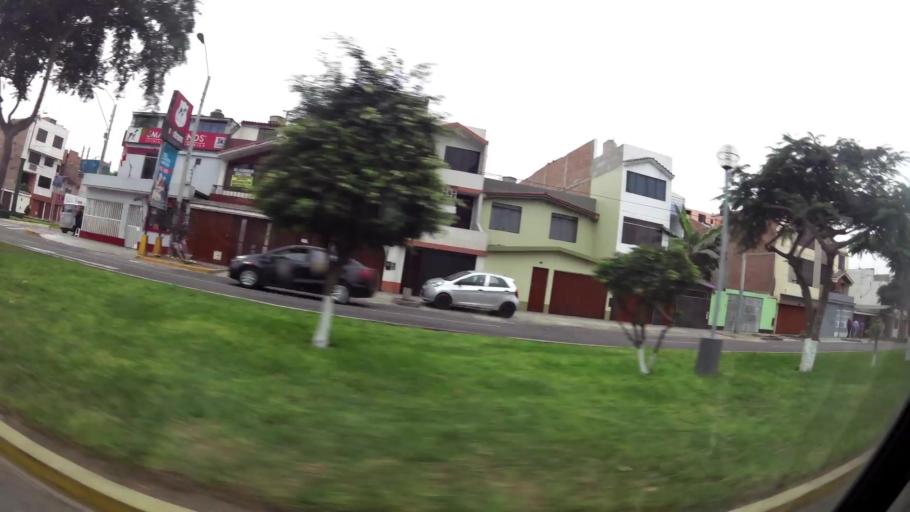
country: PE
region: Callao
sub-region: Callao
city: Callao
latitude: -12.0650
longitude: -77.1043
